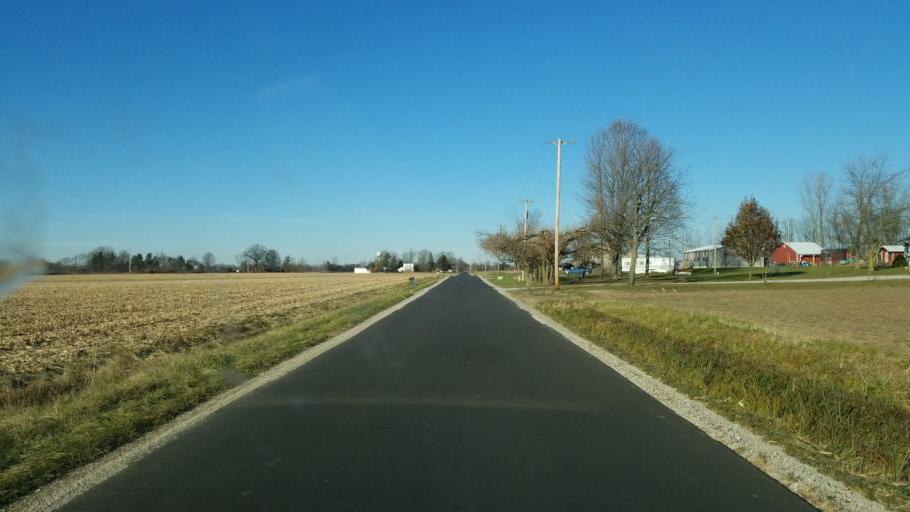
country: US
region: Ohio
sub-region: Morrow County
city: Cardington
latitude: 40.4812
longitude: -82.9031
